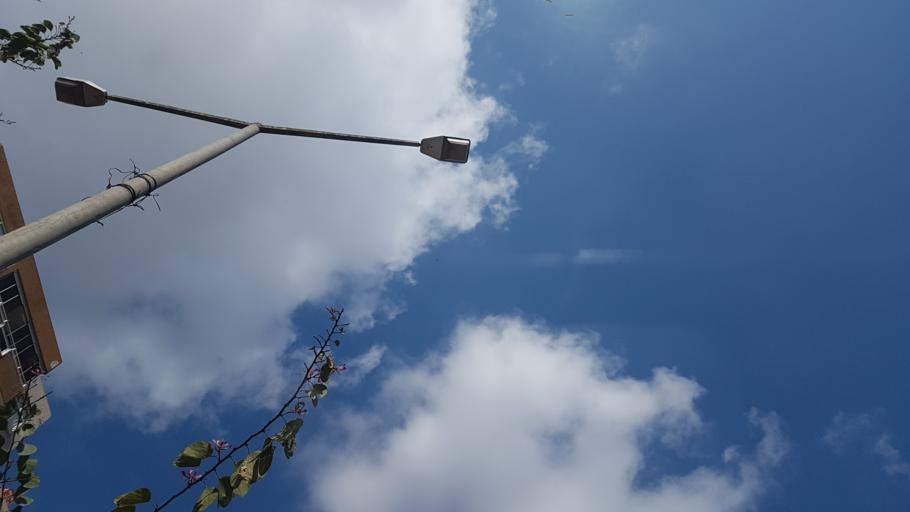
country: TR
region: Adana
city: Adana
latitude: 37.0401
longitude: 35.3024
